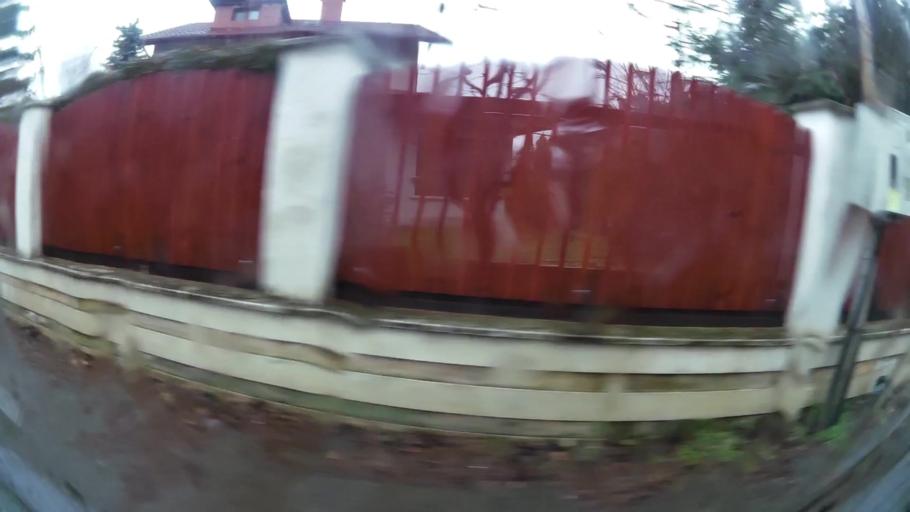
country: BG
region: Sofia-Capital
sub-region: Stolichna Obshtina
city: Sofia
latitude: 42.6268
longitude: 23.3646
